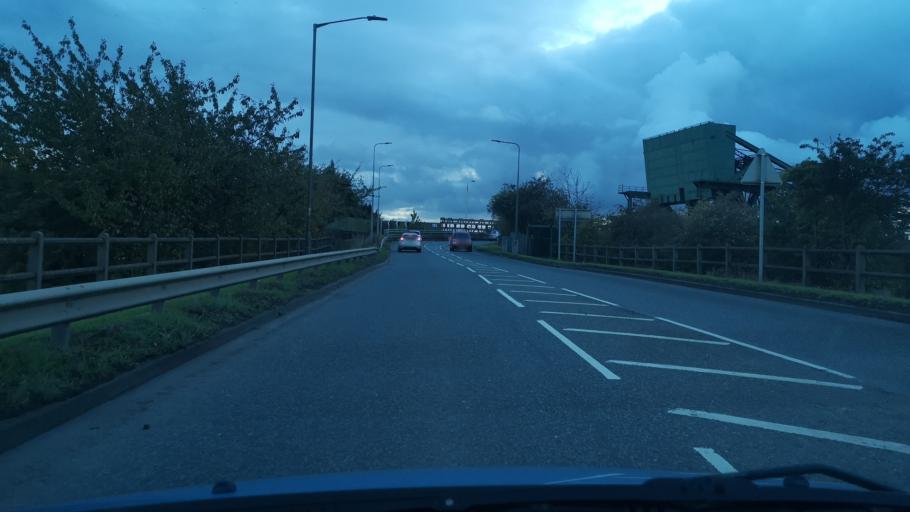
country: GB
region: England
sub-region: North Lincolnshire
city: Gunness
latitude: 53.5868
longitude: -0.7291
